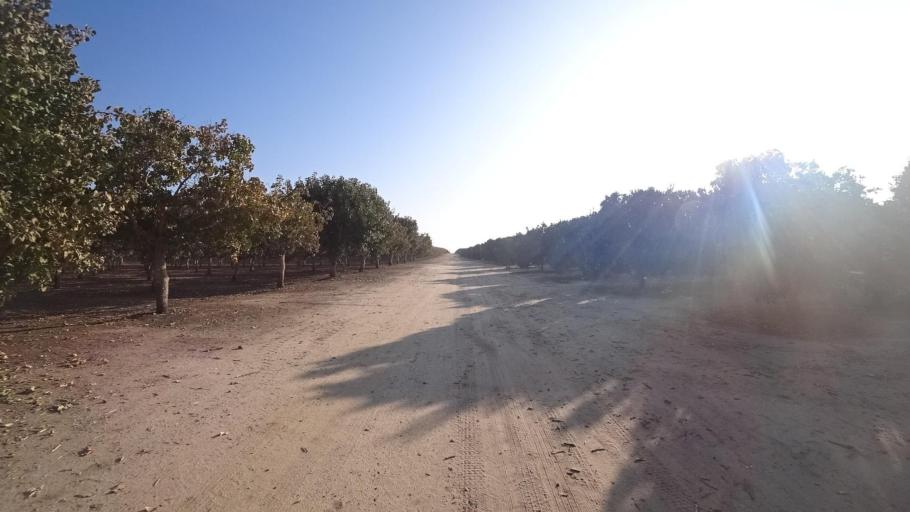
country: US
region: California
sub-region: Tulare County
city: Richgrove
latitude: 35.7763
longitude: -119.0883
